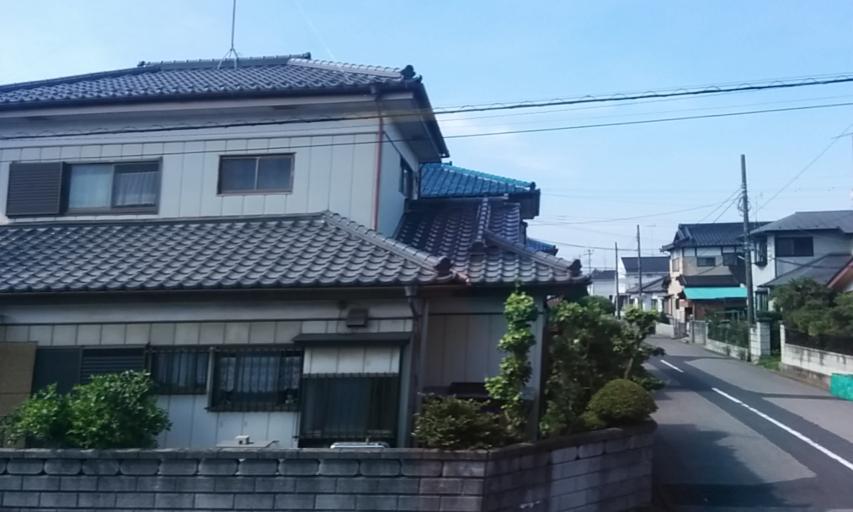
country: JP
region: Saitama
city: Kazo
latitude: 36.1155
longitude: 139.6168
